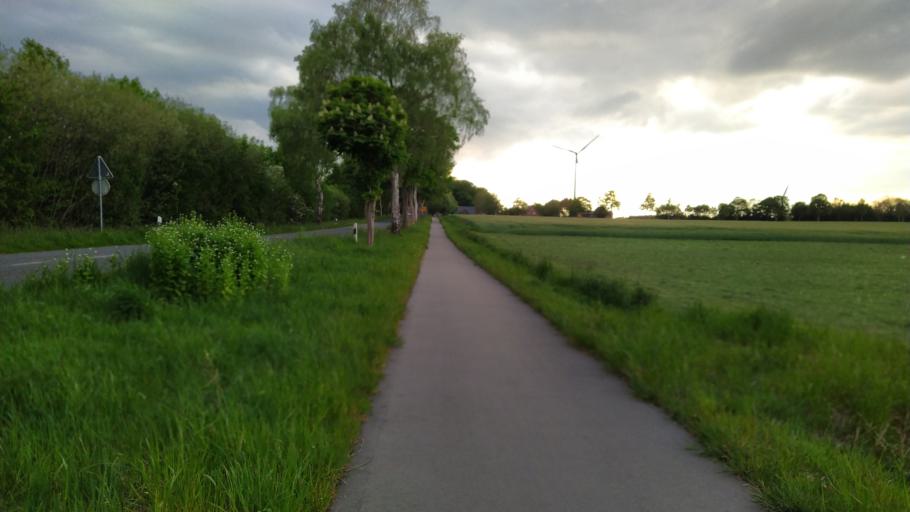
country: DE
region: Lower Saxony
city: Ahlerstedt
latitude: 53.3954
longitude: 9.4095
